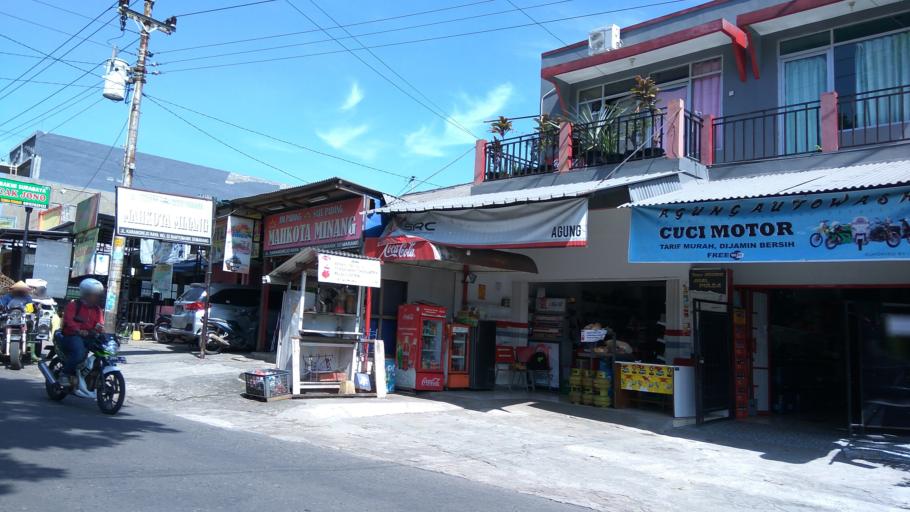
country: ID
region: Central Java
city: Ungaran
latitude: -7.0752
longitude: 110.4172
